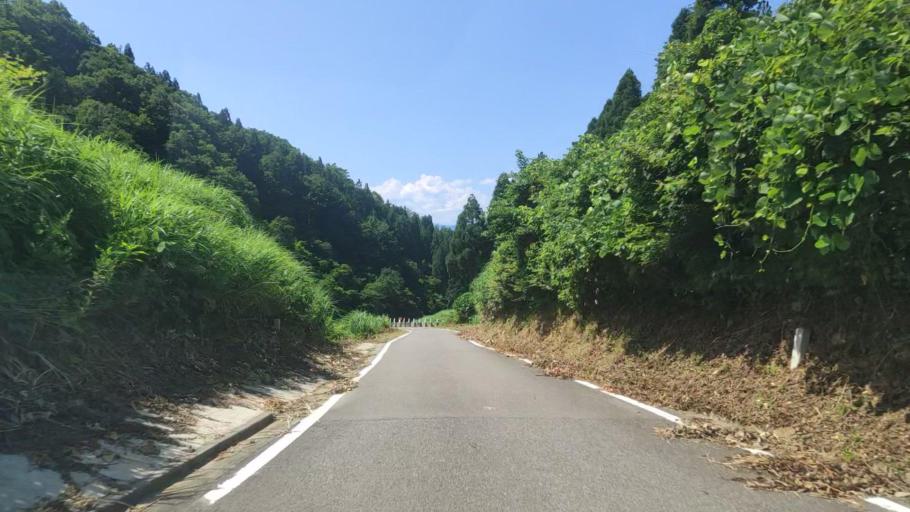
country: JP
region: Fukui
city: Katsuyama
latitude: 36.1321
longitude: 136.5133
